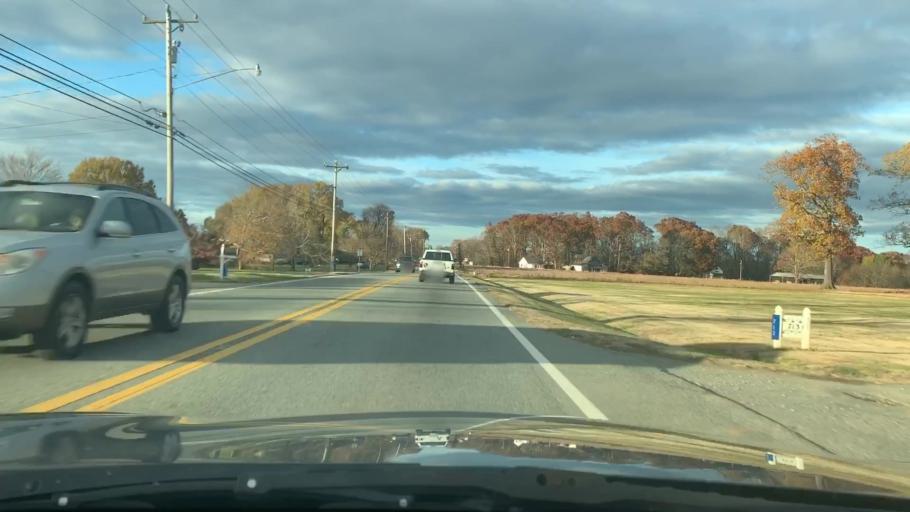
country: US
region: North Carolina
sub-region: Alamance County
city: Green Level
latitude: 36.1068
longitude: -79.3529
